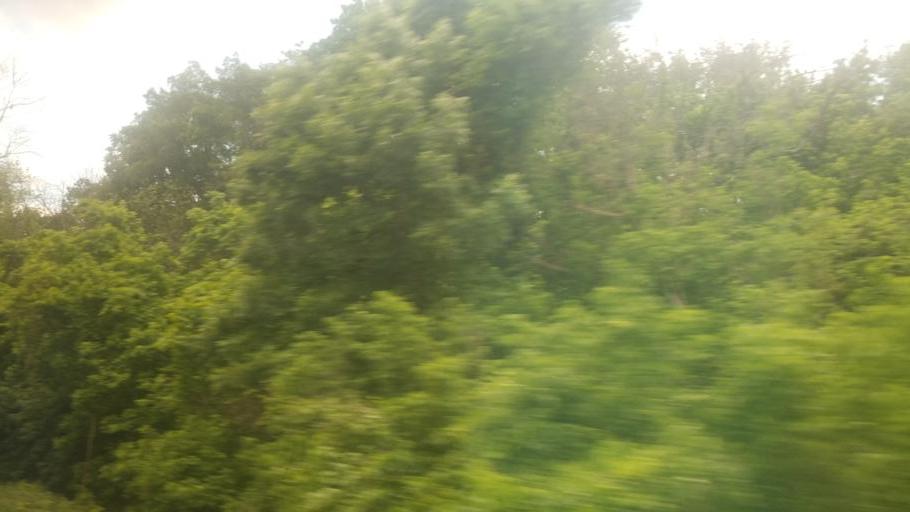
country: US
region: Maryland
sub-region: Frederick County
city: Brunswick
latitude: 39.3073
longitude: -77.6105
